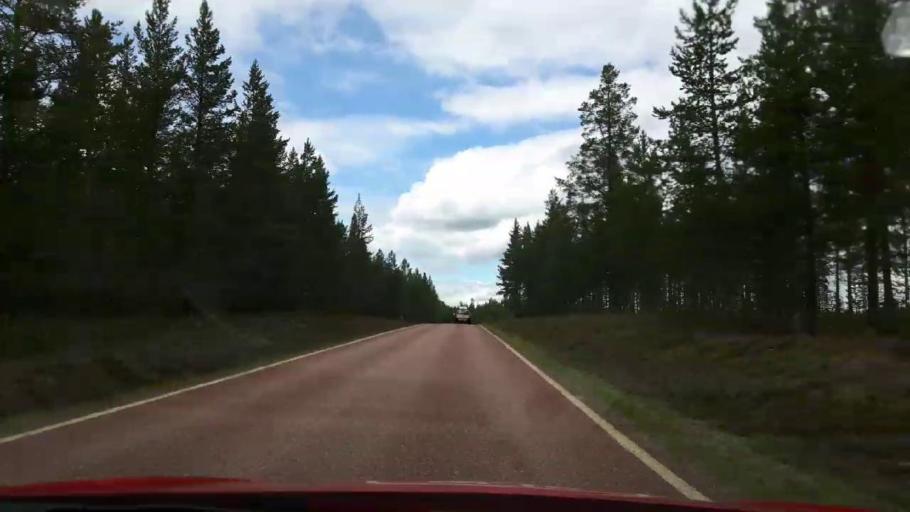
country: NO
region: Hedmark
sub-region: Trysil
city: Innbygda
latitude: 61.8462
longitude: 12.9548
